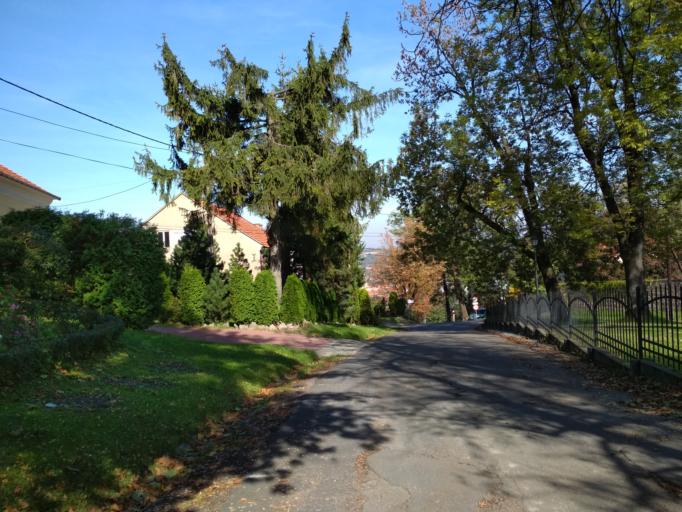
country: PL
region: Lesser Poland Voivodeship
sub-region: Powiat wadowicki
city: Kalwaria Zebrzydowska
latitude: 49.8609
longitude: 19.6740
